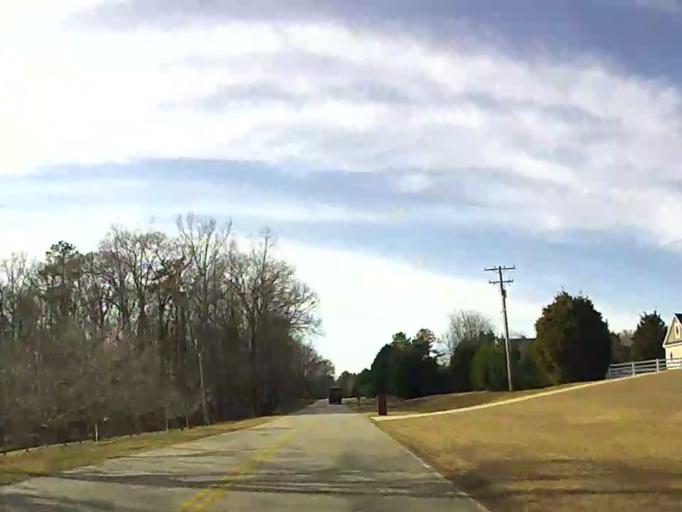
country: US
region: Georgia
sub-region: Bibb County
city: West Point
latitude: 32.9375
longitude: -83.7858
